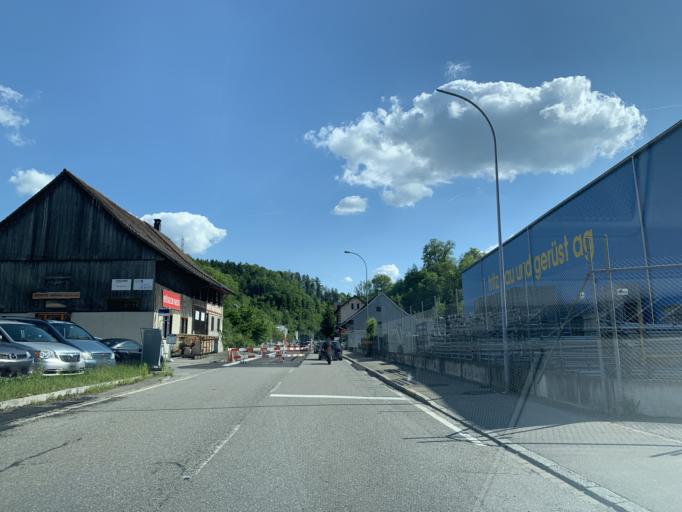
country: CH
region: Zurich
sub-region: Bezirk Pfaeffikon
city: Effretikon / Watt
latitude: 47.4432
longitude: 8.7042
